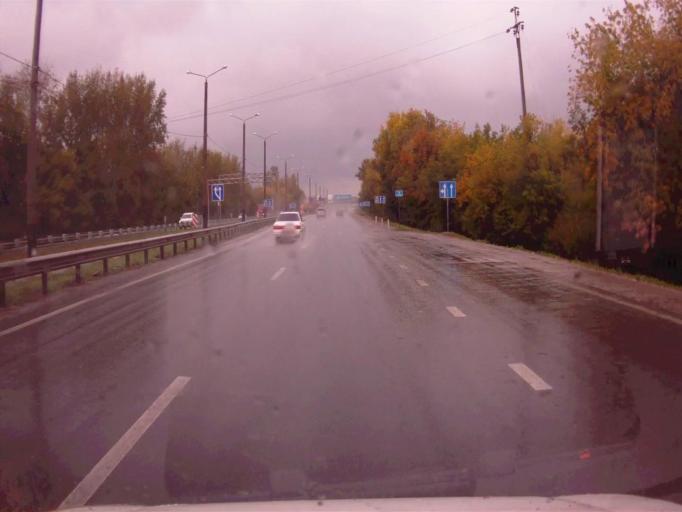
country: RU
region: Chelyabinsk
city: Dolgoderevenskoye
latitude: 55.2581
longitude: 61.3509
